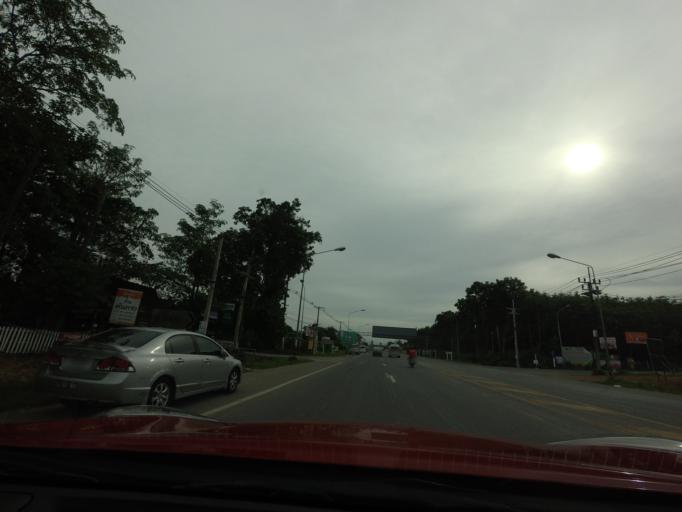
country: TH
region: Songkhla
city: Khlong Hoi Khong
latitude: 6.9406
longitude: 100.4025
